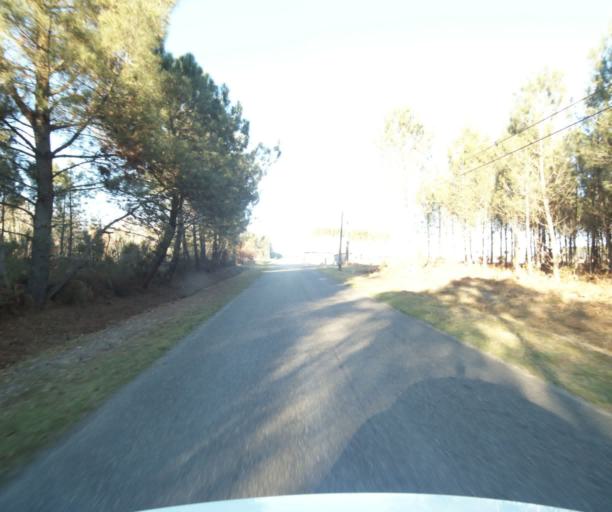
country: FR
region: Aquitaine
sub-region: Departement des Landes
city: Gabarret
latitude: 44.1224
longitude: -0.0968
